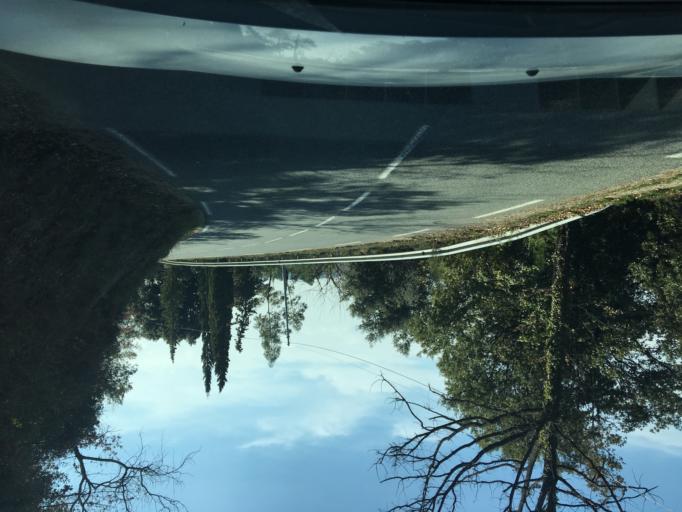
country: FR
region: Provence-Alpes-Cote d'Azur
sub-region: Departement du Var
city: Bargemon
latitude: 43.6044
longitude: 6.5500
